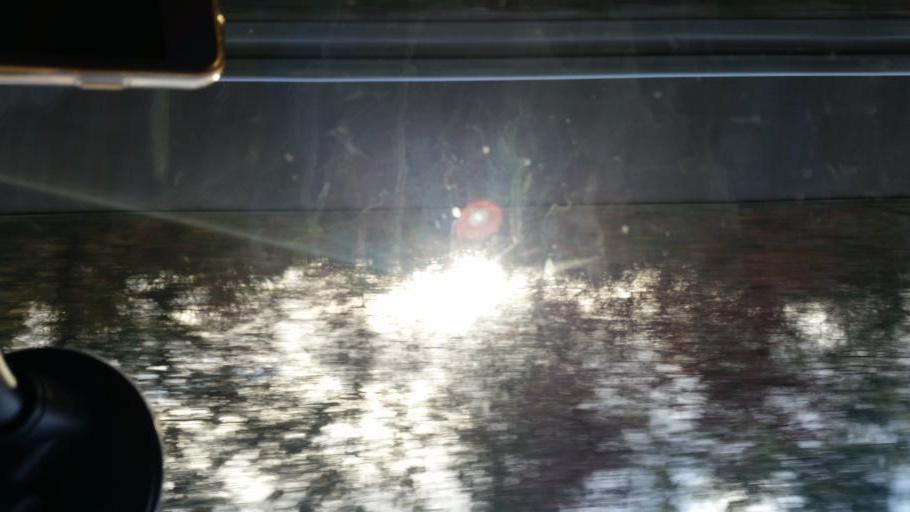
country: IE
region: Ulster
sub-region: County Monaghan
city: Carrickmacross
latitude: 53.9596
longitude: -6.6818
